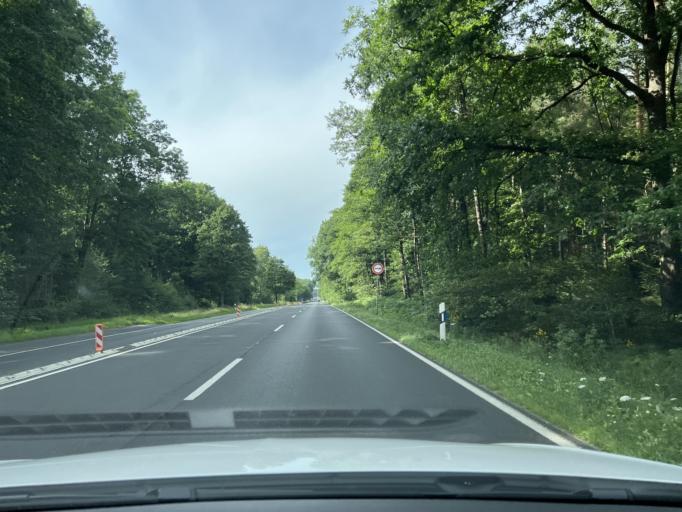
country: DE
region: North Rhine-Westphalia
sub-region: Regierungsbezirk Koln
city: Roetgen
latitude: 50.6718
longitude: 6.1852
